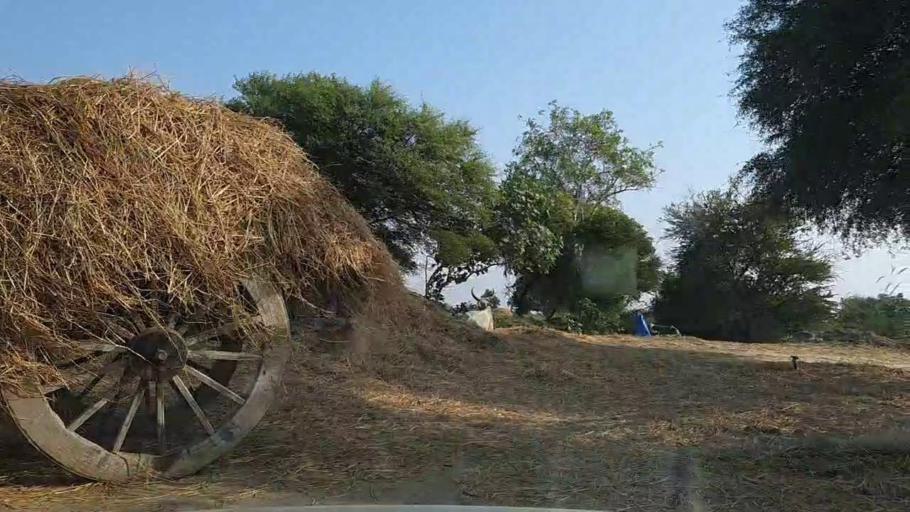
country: PK
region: Sindh
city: Mirpur Sakro
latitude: 24.5913
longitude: 67.6461
